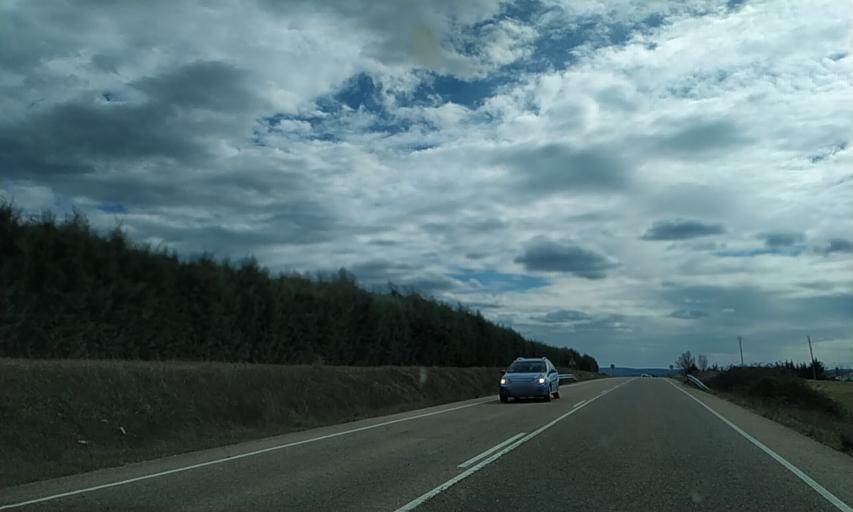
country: ES
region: Castille and Leon
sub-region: Provincia de Salamanca
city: Ciudad Rodrigo
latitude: 40.5694
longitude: -6.5457
